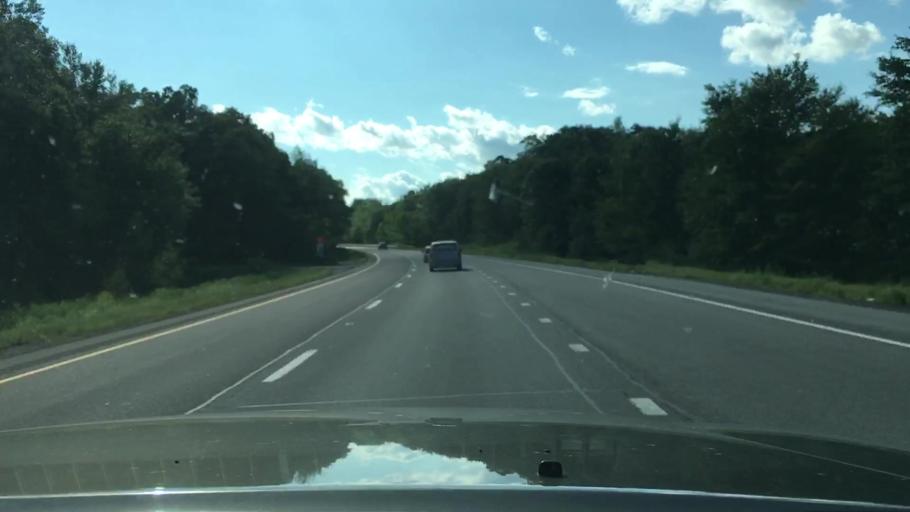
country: US
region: Pennsylvania
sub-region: Pike County
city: Hemlock Farms
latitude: 41.3680
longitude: -75.1325
